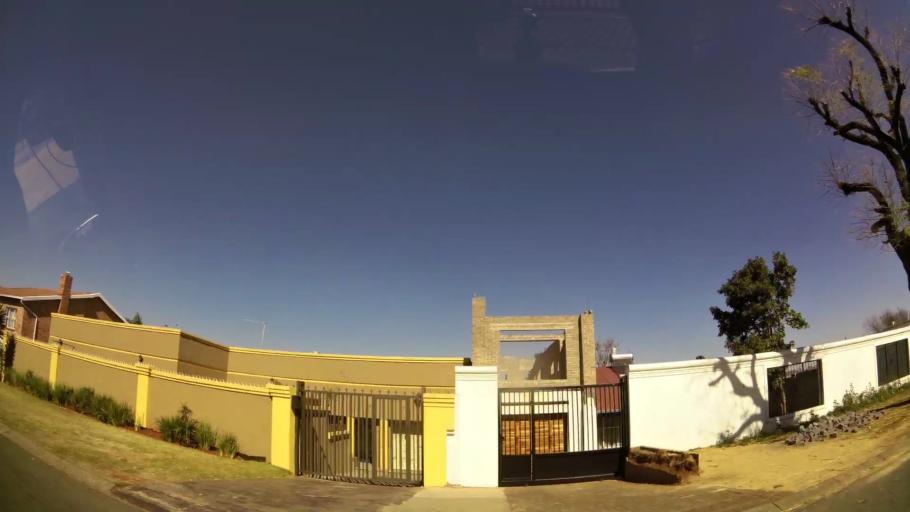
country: ZA
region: Gauteng
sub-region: City of Johannesburg Metropolitan Municipality
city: Roodepoort
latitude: -26.1894
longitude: 27.9548
